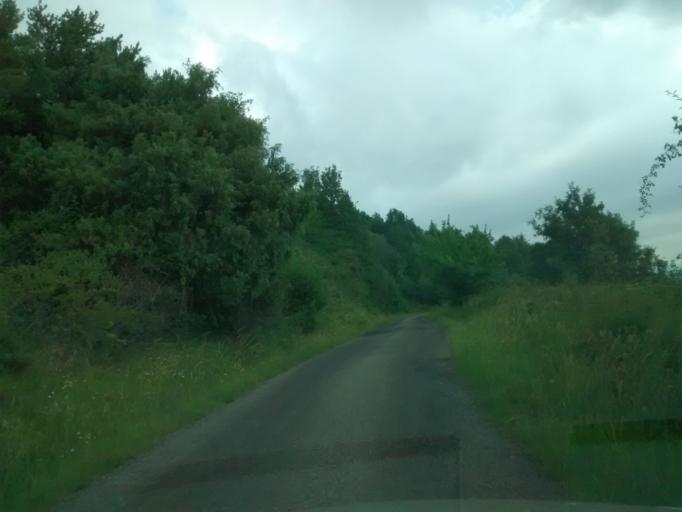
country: ES
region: Aragon
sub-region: Provincia de Huesca
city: Puertolas
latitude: 42.5566
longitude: 0.1385
